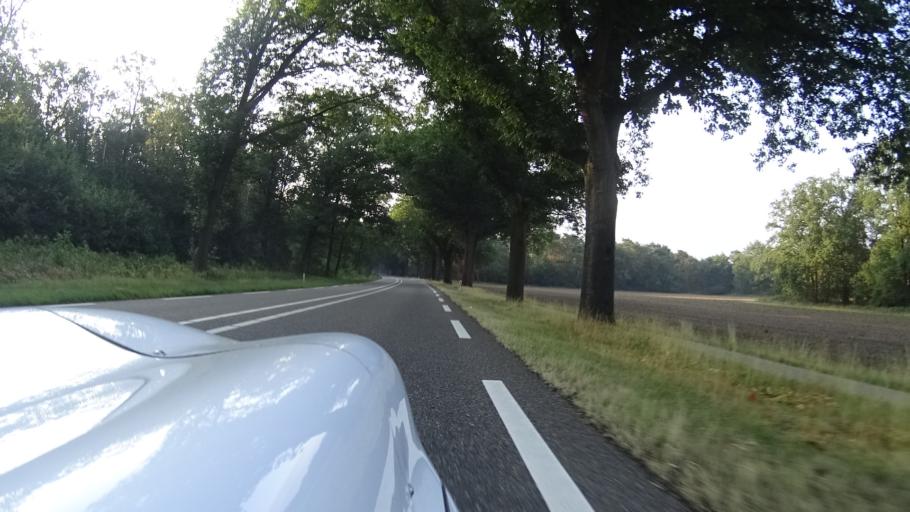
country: NL
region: Limburg
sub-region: Gemeente Bergen
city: Wellerlooi
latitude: 51.5224
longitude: 6.1450
